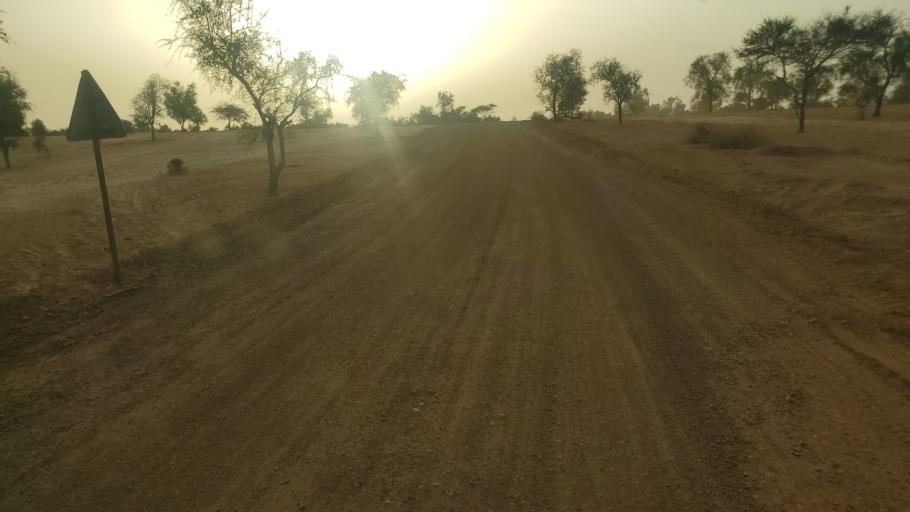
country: SN
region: Louga
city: Dara
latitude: 15.3780
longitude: -15.6000
